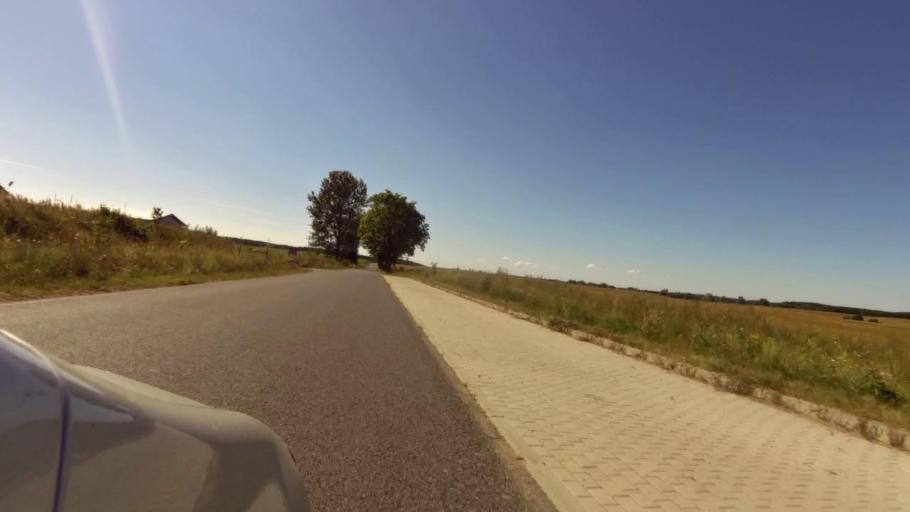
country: PL
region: West Pomeranian Voivodeship
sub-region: Powiat szczecinecki
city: Bialy Bor
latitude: 53.8183
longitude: 16.7889
